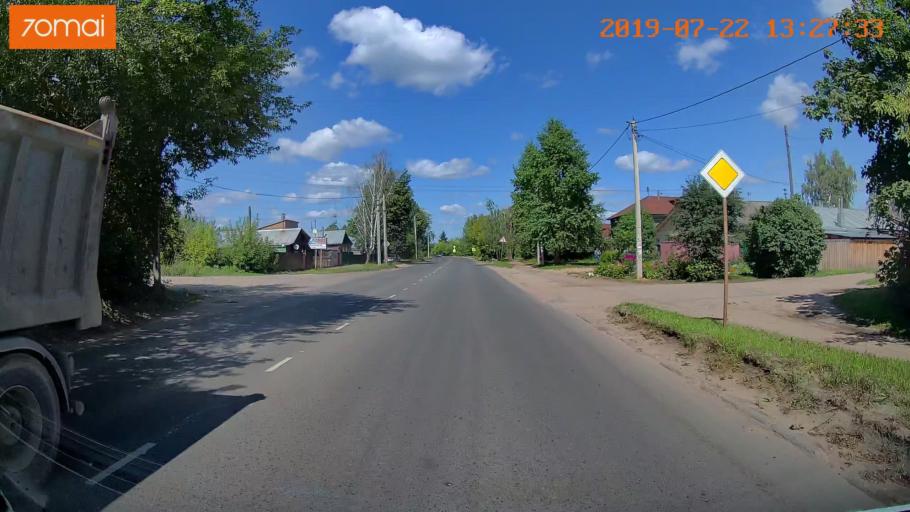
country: RU
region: Ivanovo
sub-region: Gorod Ivanovo
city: Ivanovo
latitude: 57.0360
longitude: 40.9504
